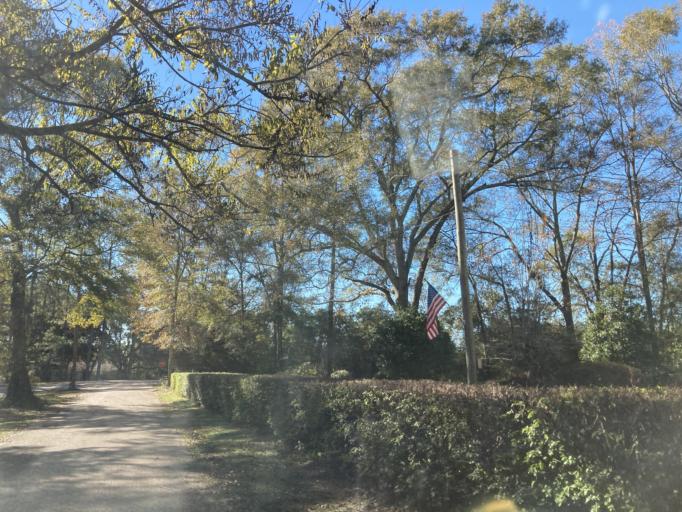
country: US
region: Mississippi
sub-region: Lamar County
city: Sumrall
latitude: 31.3129
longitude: -89.6199
